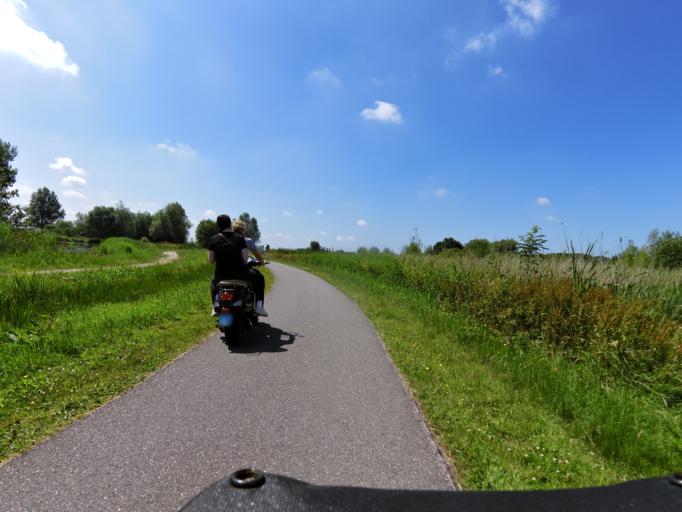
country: NL
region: South Holland
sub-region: Gemeente Delft
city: Delft
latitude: 51.9764
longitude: 4.3445
